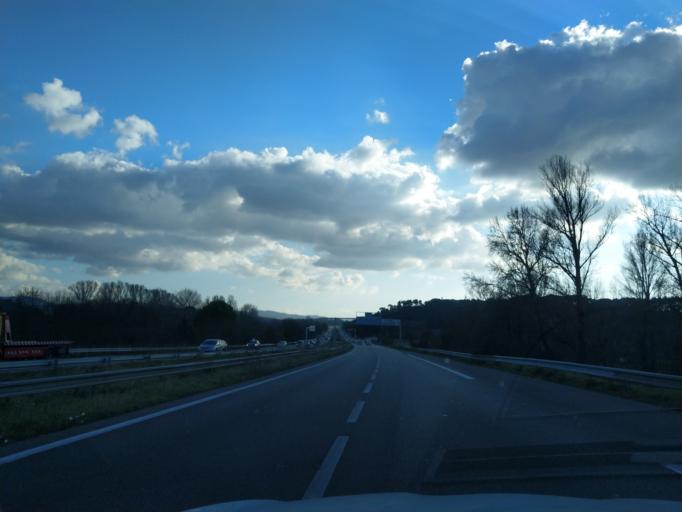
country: FR
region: Provence-Alpes-Cote d'Azur
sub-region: Departement des Bouches-du-Rhone
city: Bouc-Bel-Air
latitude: 43.4979
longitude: 5.4065
